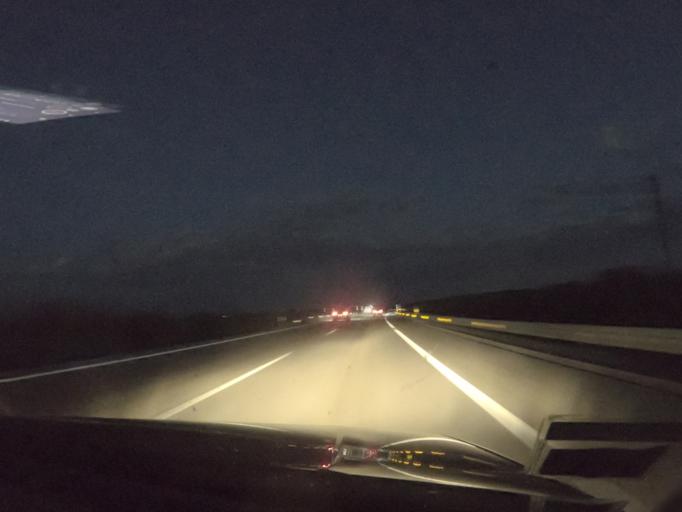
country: ES
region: Castille and Leon
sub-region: Provincia de Leon
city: Brazuelo
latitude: 42.5244
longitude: -6.1263
